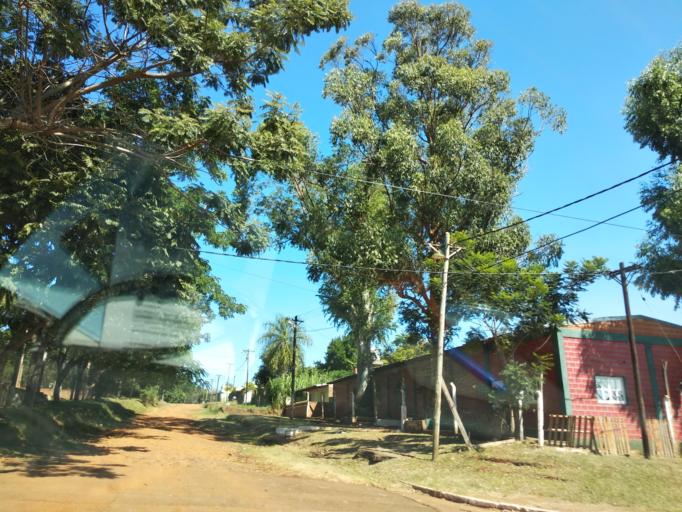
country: AR
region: Misiones
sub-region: Departamento de Capital
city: Posadas
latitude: -27.4247
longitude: -55.8826
